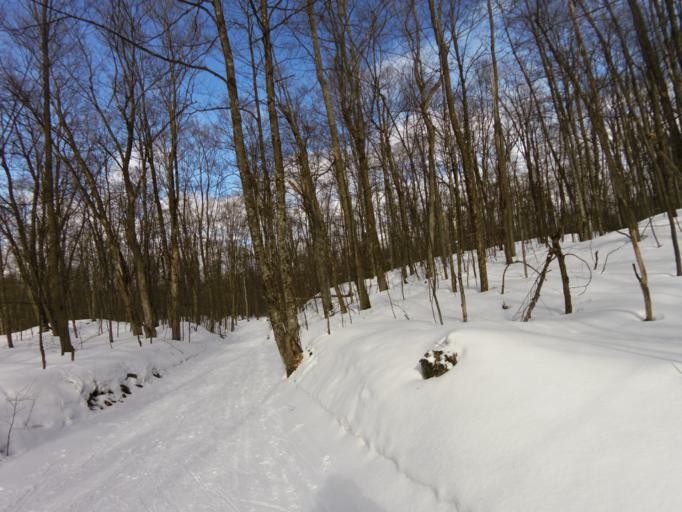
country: CA
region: Quebec
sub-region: Outaouais
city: Wakefield
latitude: 45.5314
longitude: -75.9016
